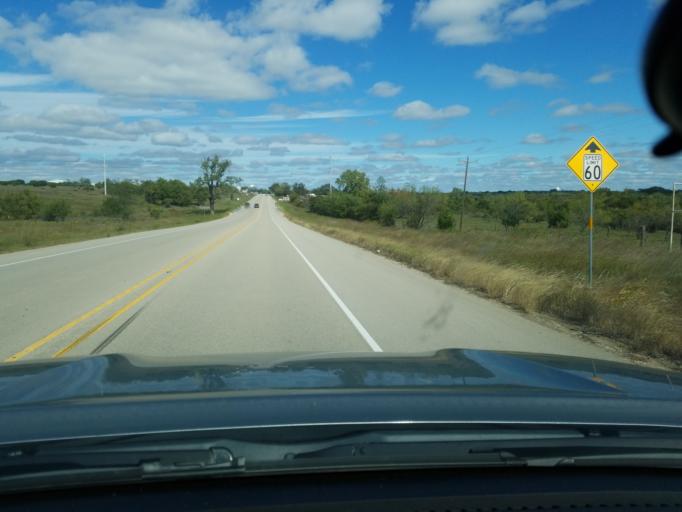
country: US
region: Texas
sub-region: Hamilton County
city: Hamilton
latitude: 31.6843
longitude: -98.1318
